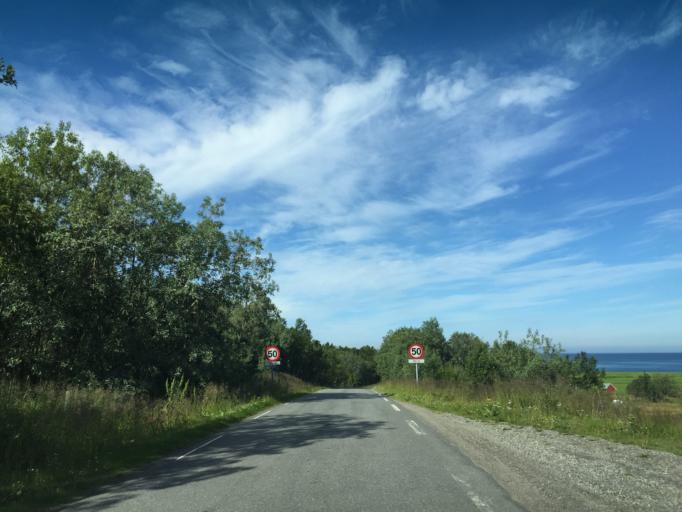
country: NO
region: Nordland
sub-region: Vagan
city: Svolvaer
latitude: 68.4012
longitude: 14.5238
